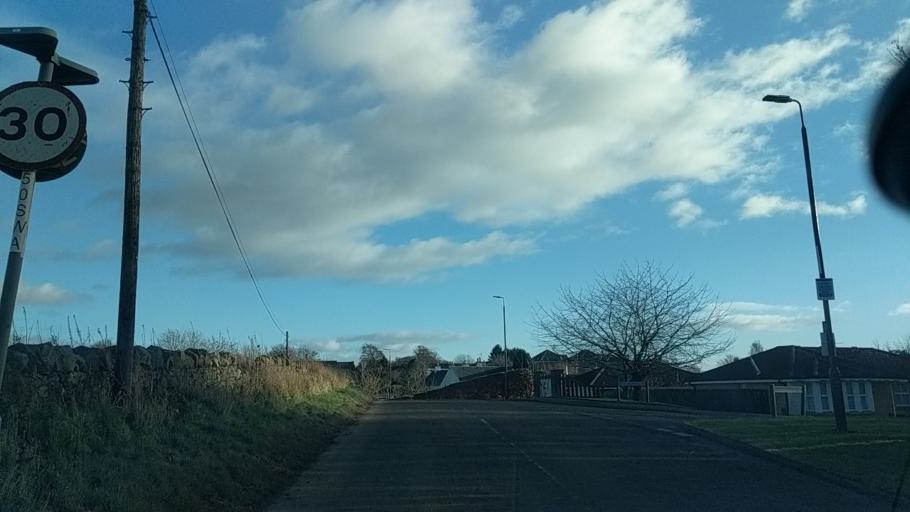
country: GB
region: Scotland
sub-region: West Lothian
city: Linlithgow
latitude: 55.9771
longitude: -3.5317
